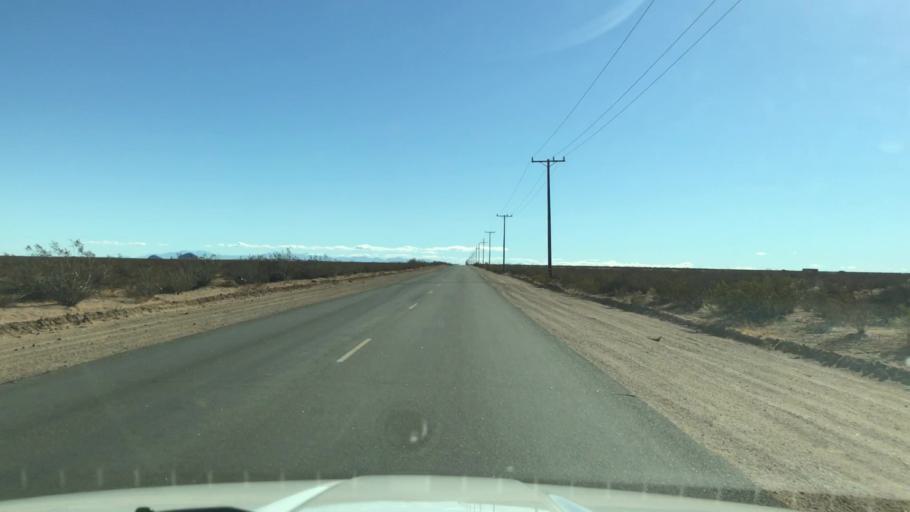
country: US
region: California
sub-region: Kern County
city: California City
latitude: 35.2089
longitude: -117.9859
